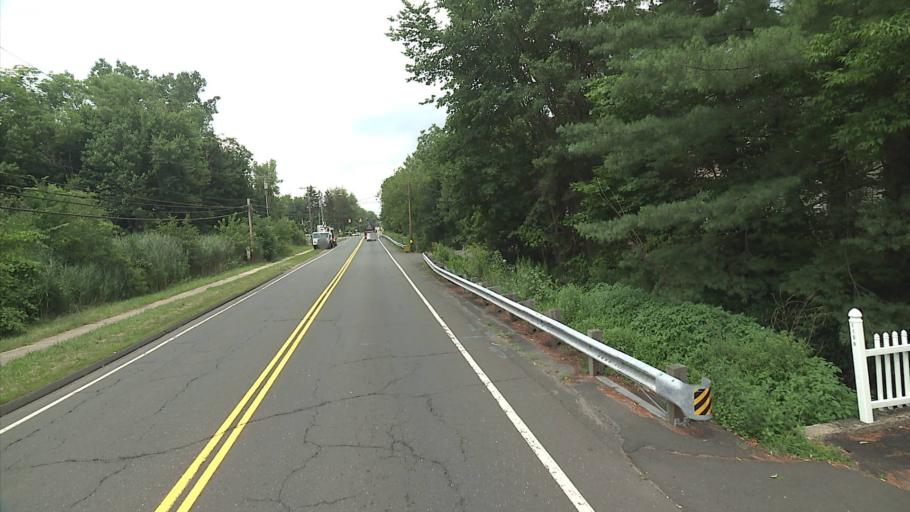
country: US
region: Connecticut
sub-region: Hartford County
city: Newington
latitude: 41.6824
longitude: -72.7305
